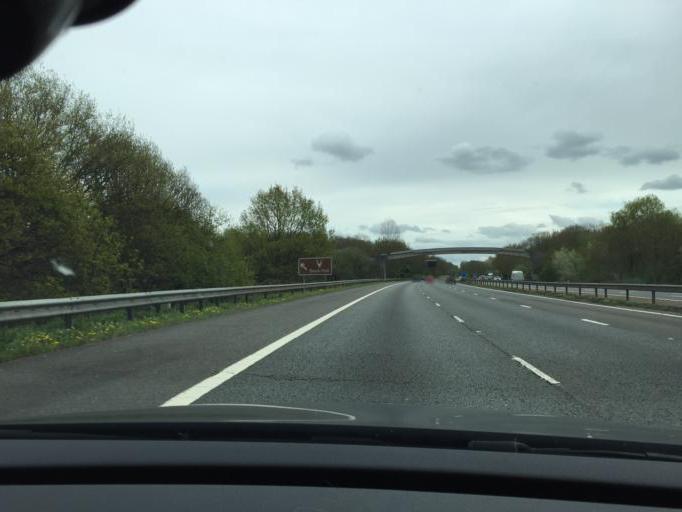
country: GB
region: England
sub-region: West Berkshire
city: Theale
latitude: 51.4532
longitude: -1.0801
